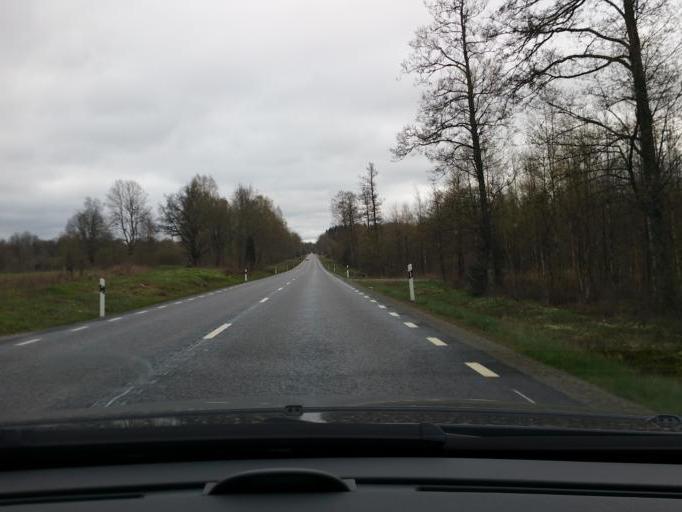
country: SE
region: Kronoberg
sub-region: Alvesta Kommun
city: Moheda
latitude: 57.0494
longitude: 14.6469
